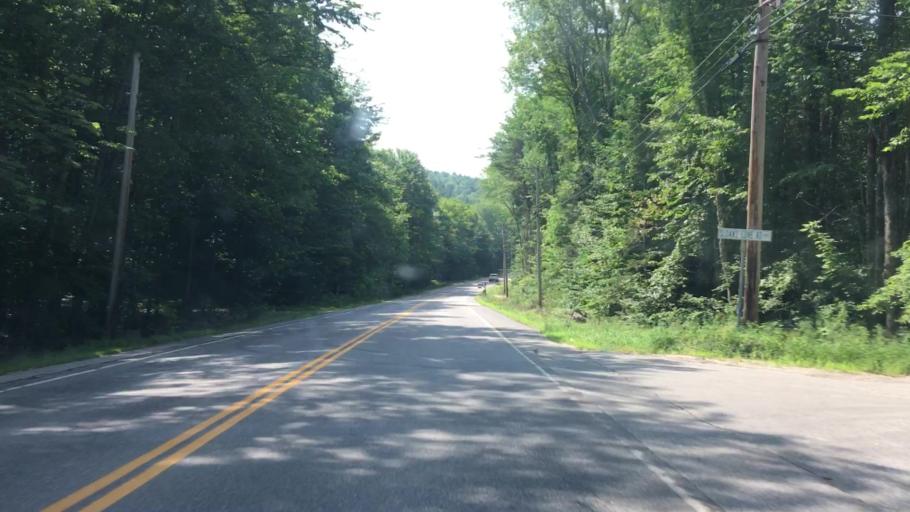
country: US
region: Maine
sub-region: Cumberland County
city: Raymond
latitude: 43.9303
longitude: -70.4378
